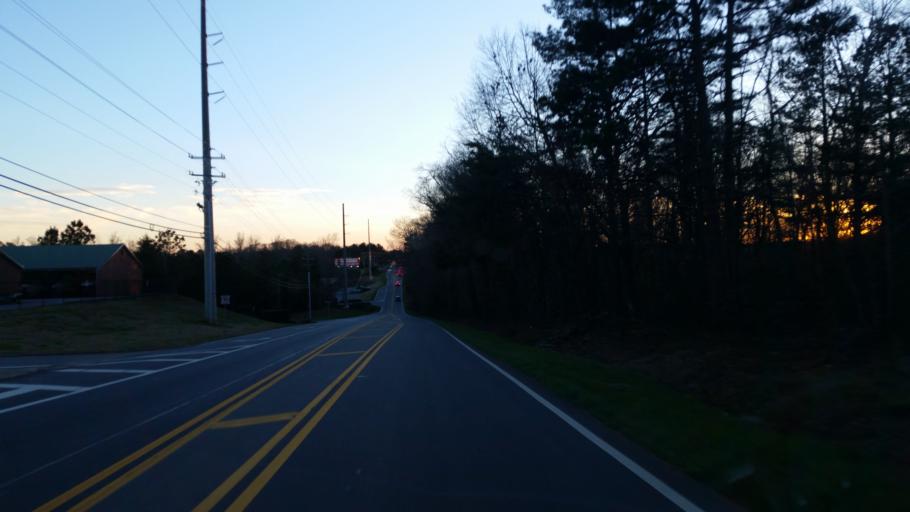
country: US
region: Georgia
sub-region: Forsyth County
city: Cumming
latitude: 34.2717
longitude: -84.0516
